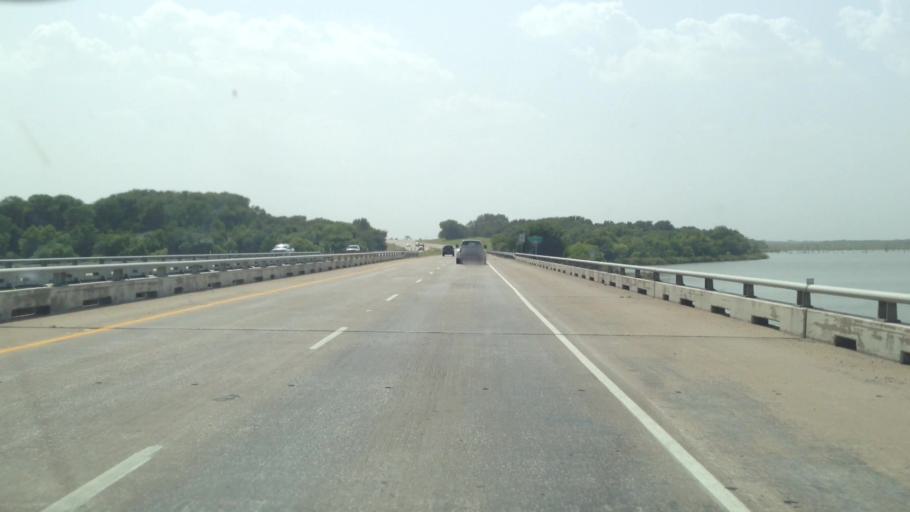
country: US
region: Texas
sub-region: Collin County
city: Princeton
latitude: 33.1632
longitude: -96.4339
